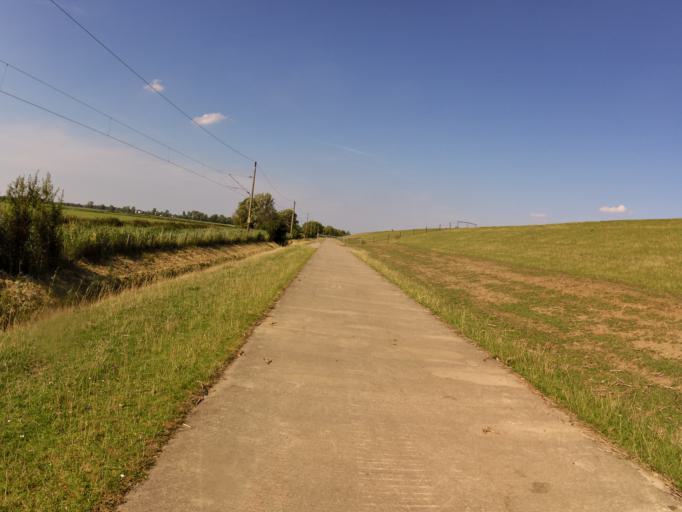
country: DE
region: Lower Saxony
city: Nordenham
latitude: 53.4516
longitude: 8.4753
